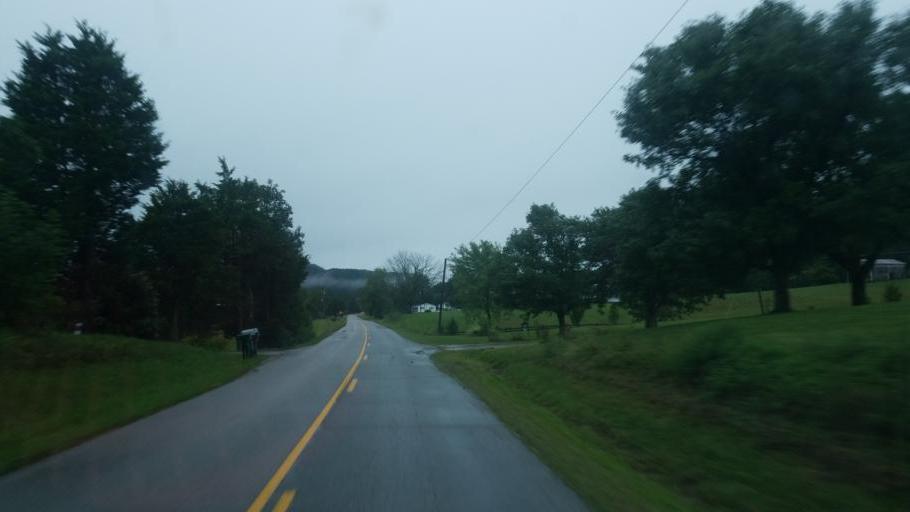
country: US
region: Kentucky
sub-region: Fleming County
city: Flemingsburg
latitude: 38.4041
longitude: -83.6333
